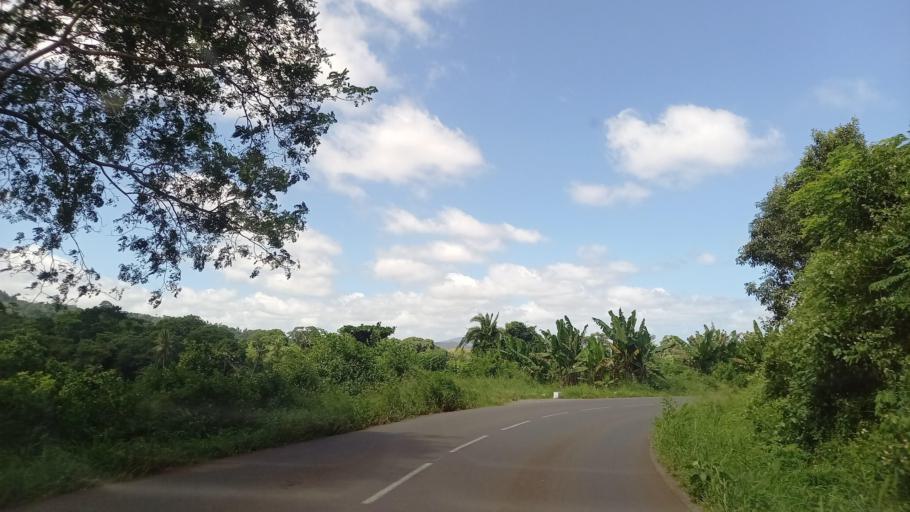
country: YT
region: Acoua
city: Acoua
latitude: -12.7476
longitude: 45.0557
